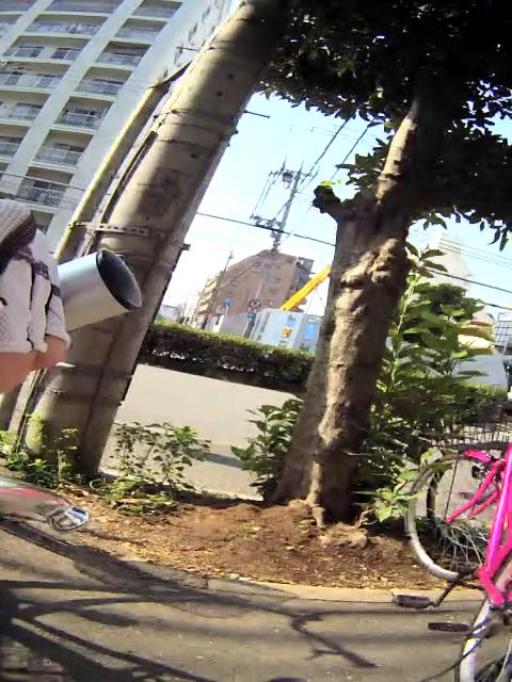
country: JP
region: Osaka
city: Suita
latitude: 34.7344
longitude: 135.4895
